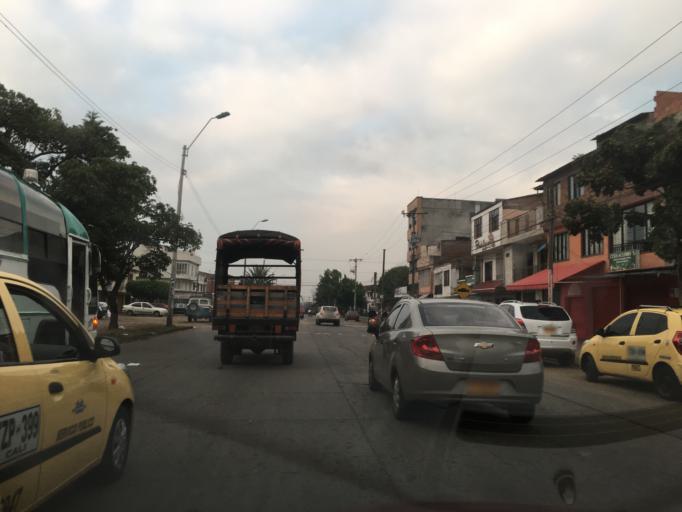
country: CO
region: Valle del Cauca
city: Cali
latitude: 3.4332
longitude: -76.5205
